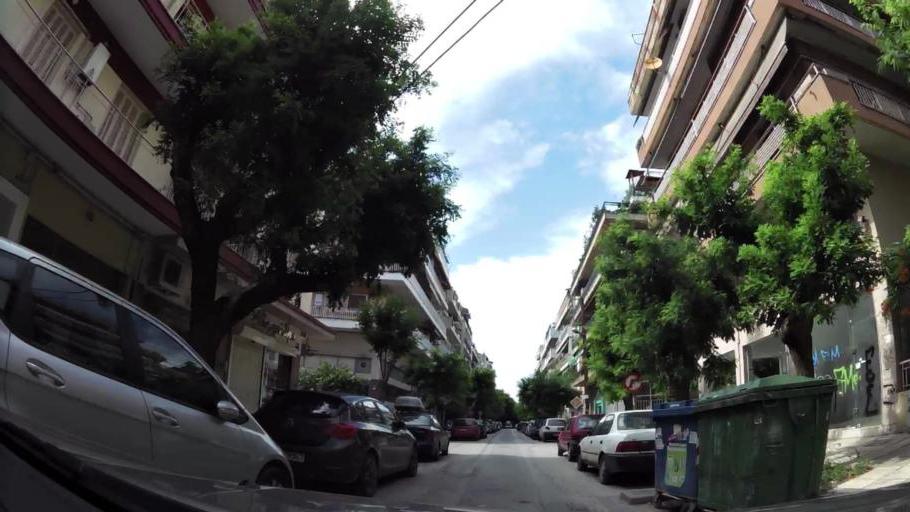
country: GR
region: Central Macedonia
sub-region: Nomos Thessalonikis
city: Kalamaria
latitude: 40.5970
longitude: 22.9584
